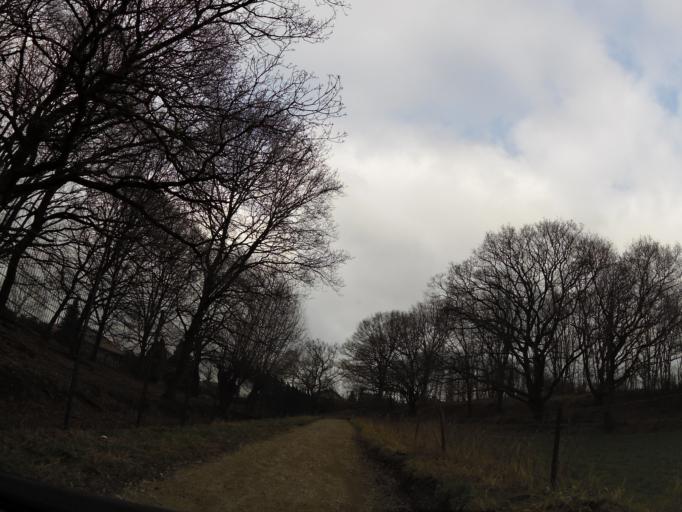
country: NL
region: Limburg
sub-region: Gemeente Kerkrade
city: Kerkrade
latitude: 50.8998
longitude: 6.0356
